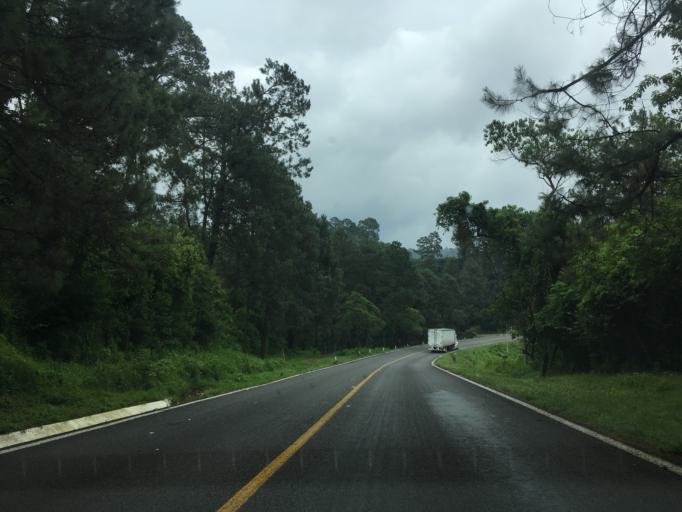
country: MX
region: Michoacan
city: Tingambato
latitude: 19.4756
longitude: -101.9292
